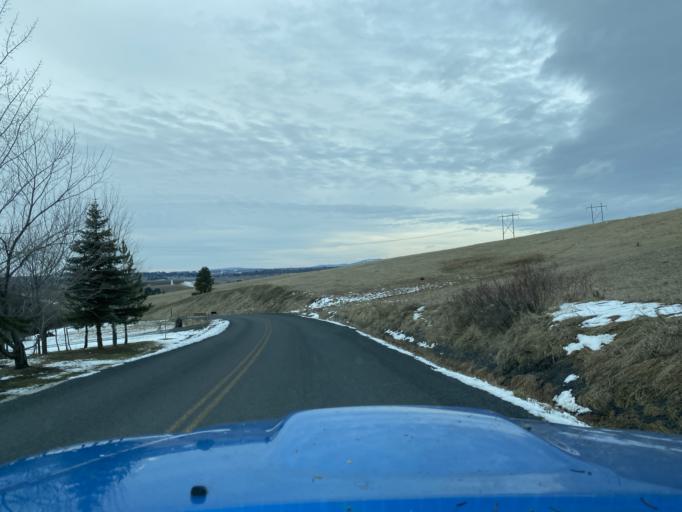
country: US
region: Idaho
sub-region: Latah County
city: Moscow
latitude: 46.7028
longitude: -116.9363
